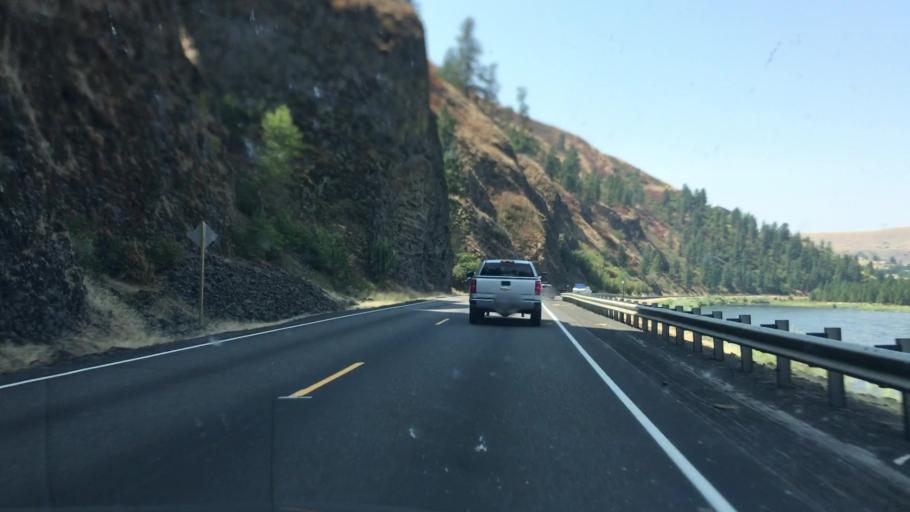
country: US
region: Idaho
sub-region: Nez Perce County
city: Lapwai
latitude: 46.4912
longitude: -116.7276
